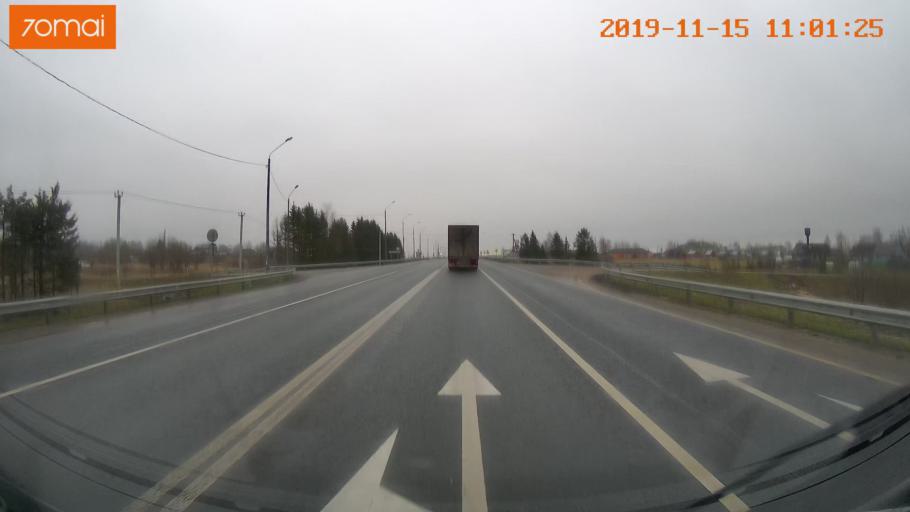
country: RU
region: Vologda
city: Chebsara
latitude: 59.1329
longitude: 38.9203
